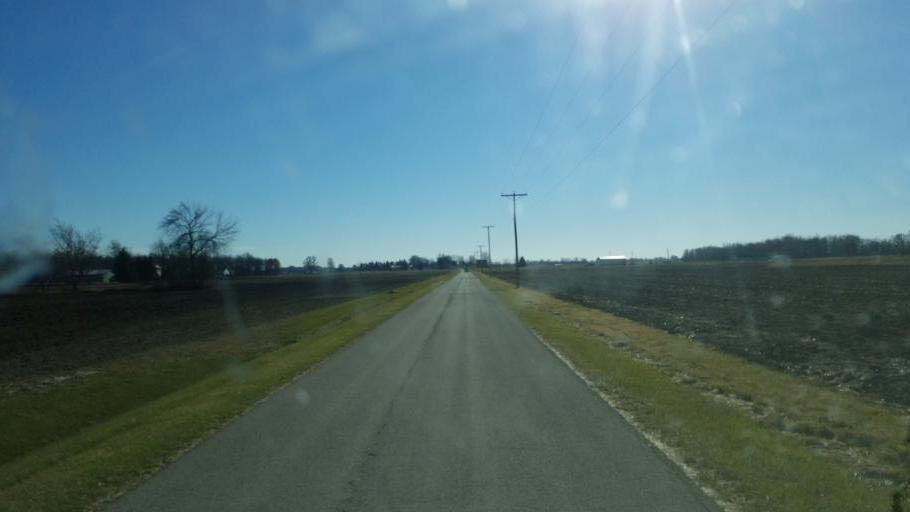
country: US
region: Ohio
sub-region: Crawford County
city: Galion
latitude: 40.7752
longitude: -82.8387
